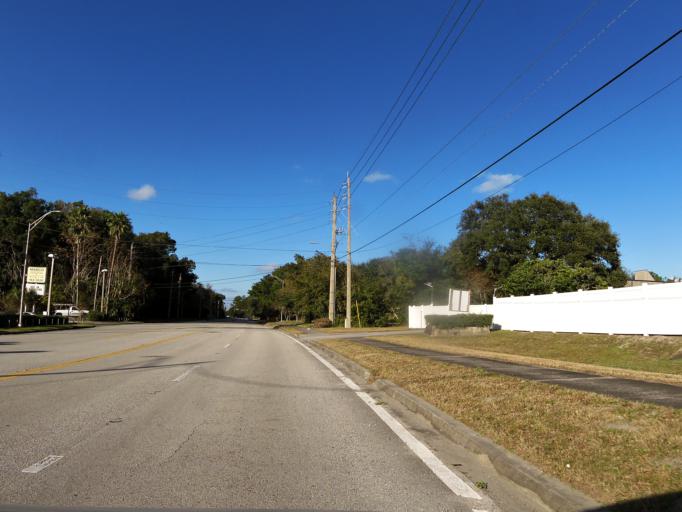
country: US
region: Florida
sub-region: Duval County
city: Jacksonville
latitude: 30.3264
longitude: -81.5601
